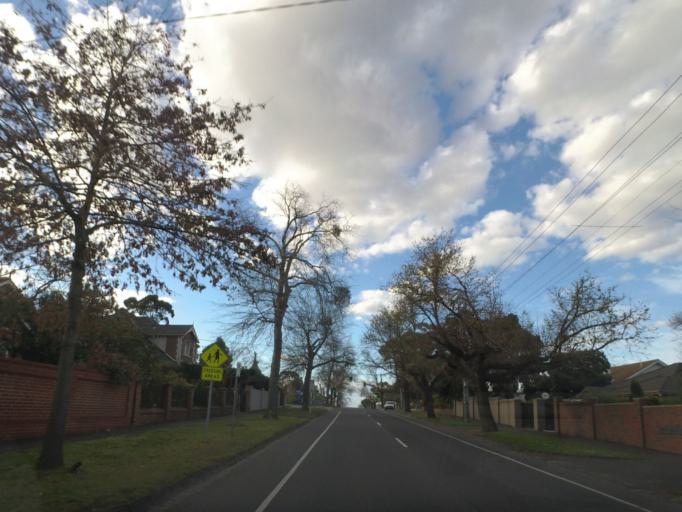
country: AU
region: Victoria
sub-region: Boroondara
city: Canterbury
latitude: -37.8163
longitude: 145.0806
